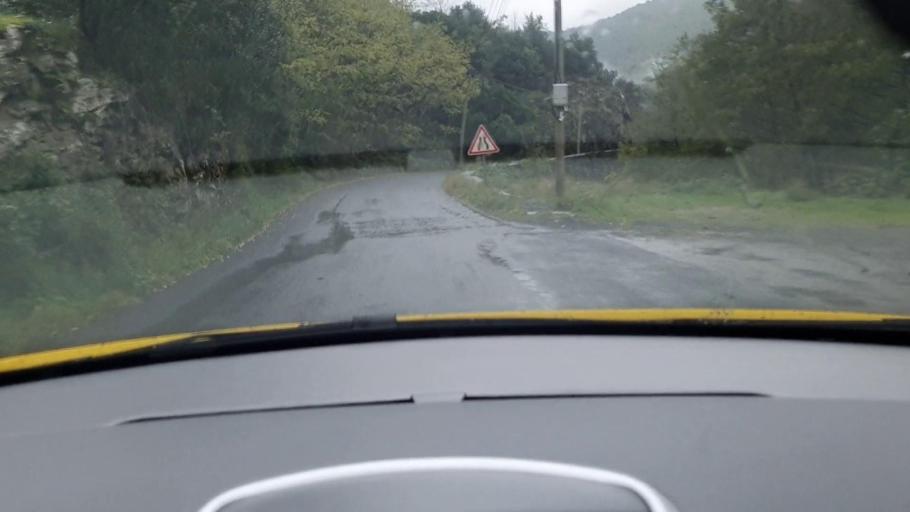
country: FR
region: Languedoc-Roussillon
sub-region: Departement du Gard
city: Sumene
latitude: 44.0119
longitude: 3.7154
